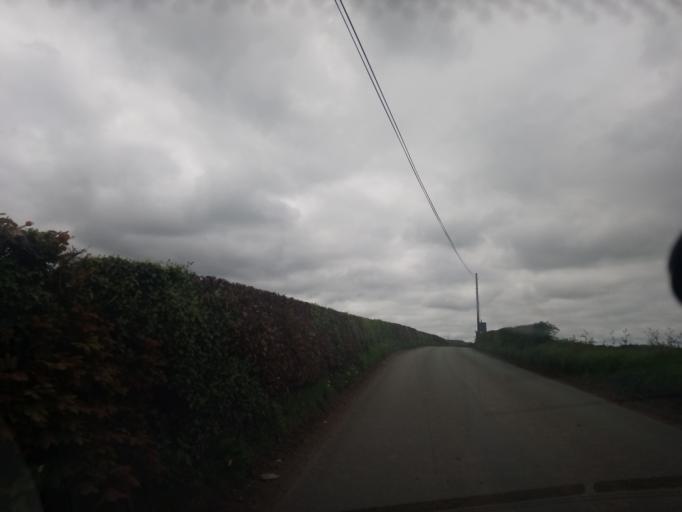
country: GB
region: England
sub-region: Shropshire
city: Stoke upon Tern
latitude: 52.8476
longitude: -2.5517
